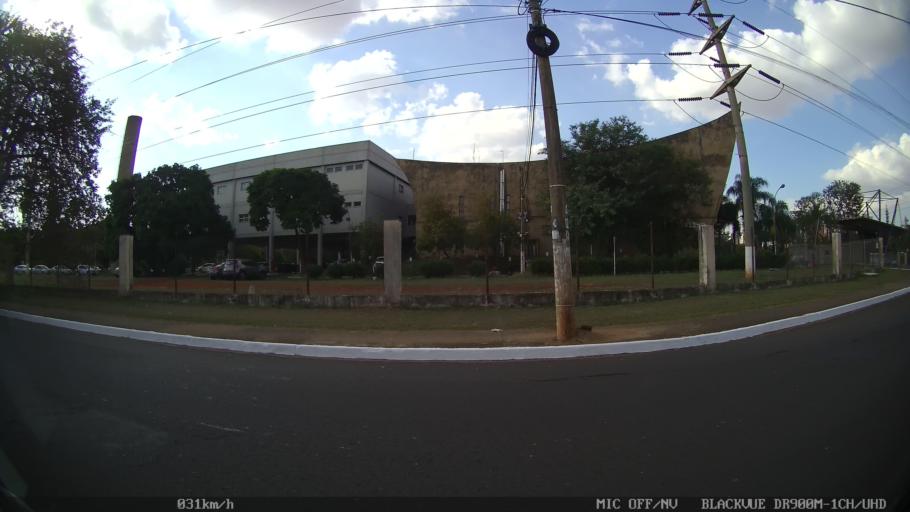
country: BR
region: Sao Paulo
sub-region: Ribeirao Preto
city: Ribeirao Preto
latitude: -21.1778
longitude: -47.8180
